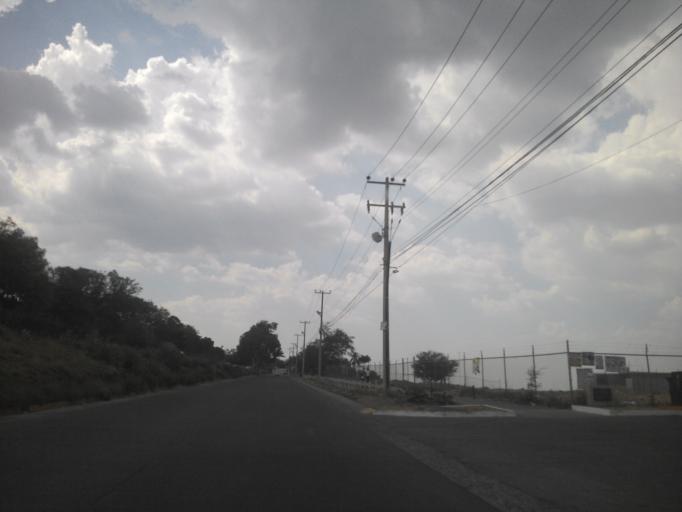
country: MX
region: Jalisco
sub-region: Tlajomulco de Zuniga
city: La Tijera
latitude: 20.6151
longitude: -103.4011
